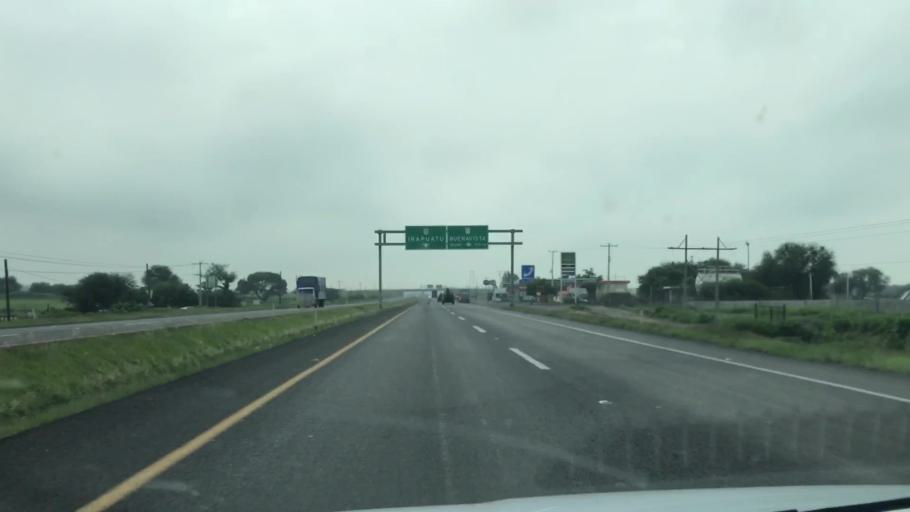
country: MX
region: Guanajuato
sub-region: Penjamo
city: Mezquite de Luna
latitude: 20.3841
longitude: -101.8853
